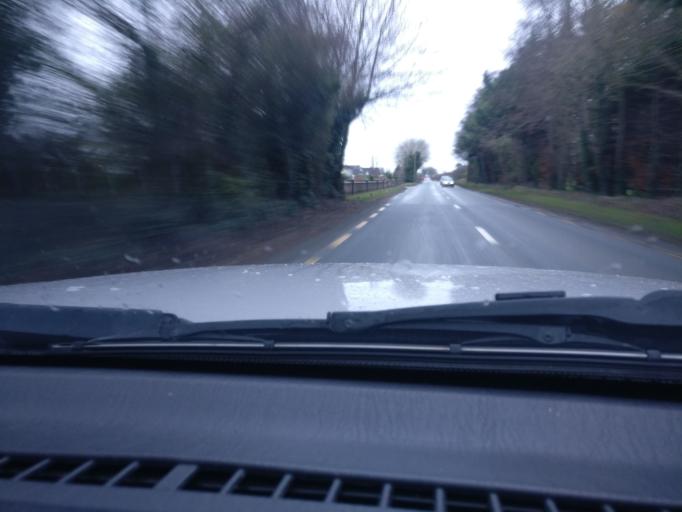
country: IE
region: Leinster
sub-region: An Mhi
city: Trim
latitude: 53.5180
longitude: -6.8307
